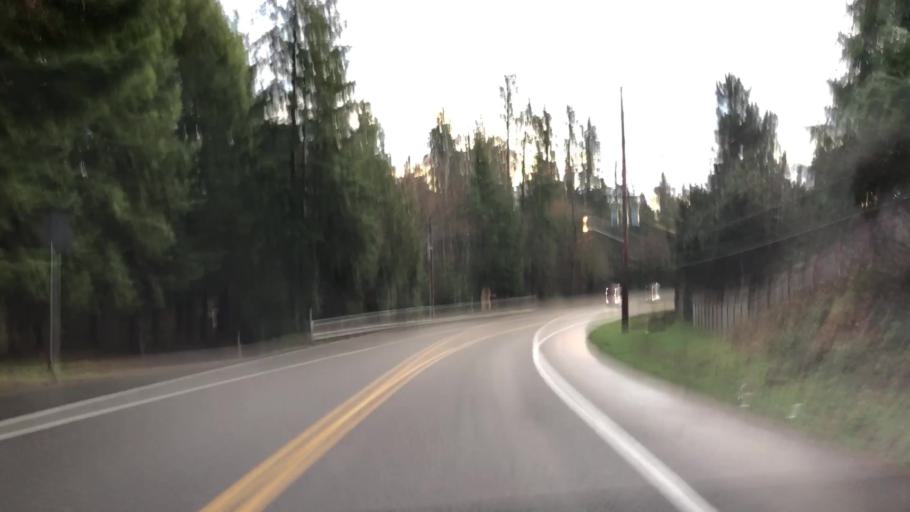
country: US
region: Washington
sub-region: King County
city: City of Sammamish
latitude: 47.6352
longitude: -122.0388
